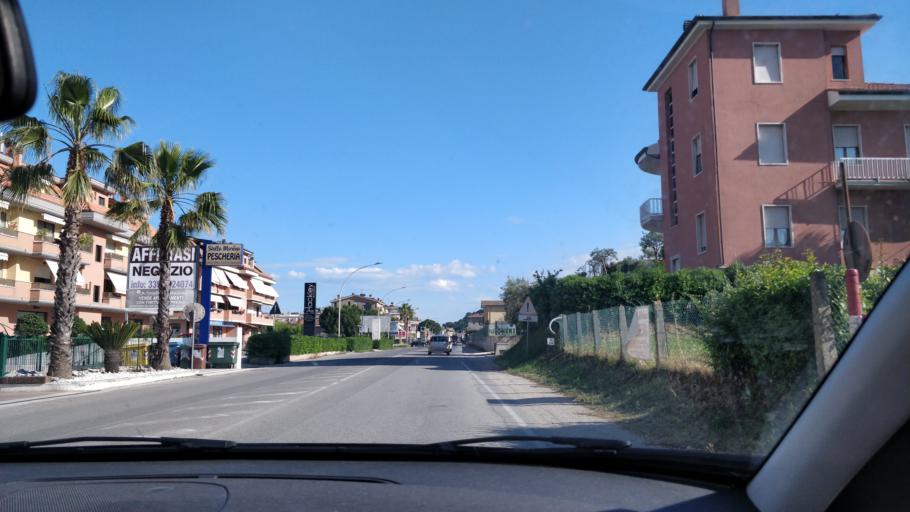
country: IT
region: The Marches
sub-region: Provincia di Ascoli Piceno
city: Cupra Marittima
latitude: 43.0346
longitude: 13.8562
